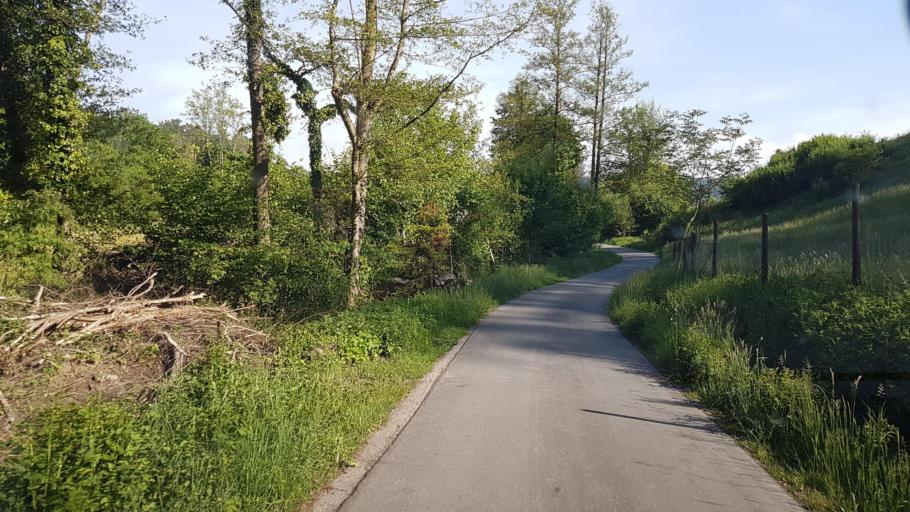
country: CH
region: Zurich
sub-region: Bezirk Dielsdorf
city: Otelfingen
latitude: 47.4695
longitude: 8.3857
